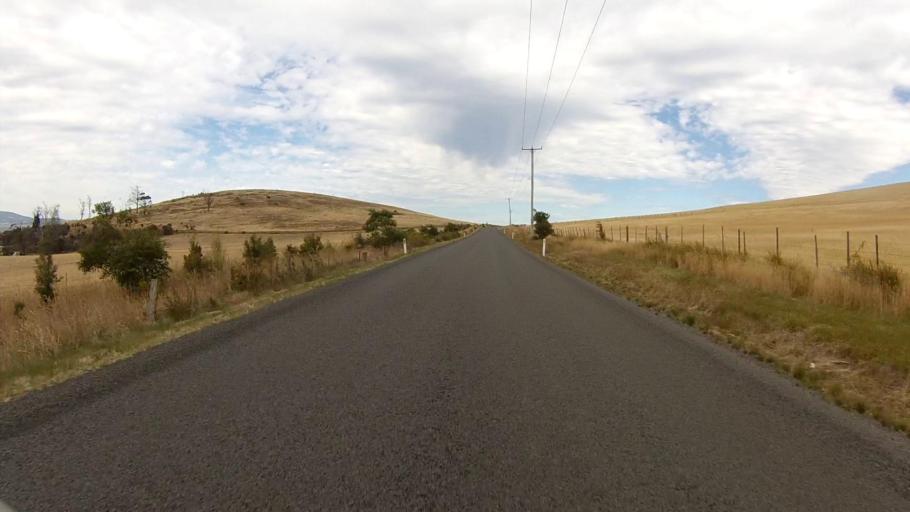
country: AU
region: Tasmania
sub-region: Sorell
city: Sorell
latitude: -42.8974
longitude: 147.7698
